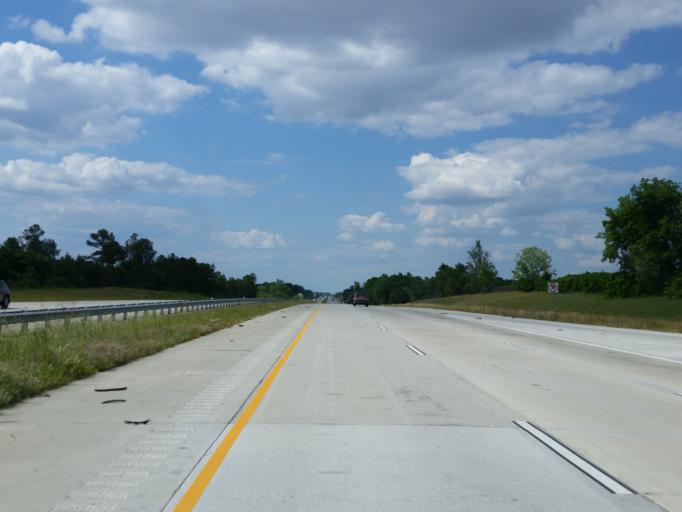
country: US
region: Georgia
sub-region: Dooly County
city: Vienna
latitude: 32.1256
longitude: -83.7604
